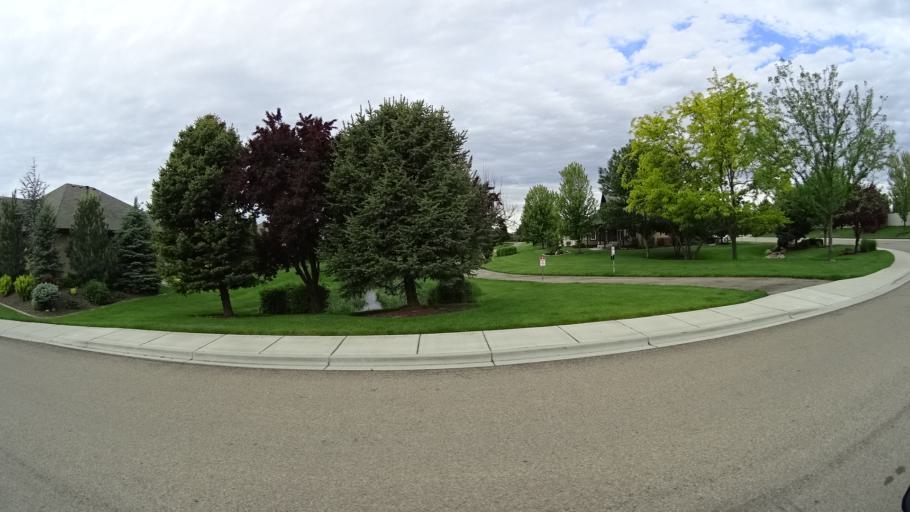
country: US
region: Idaho
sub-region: Ada County
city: Star
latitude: 43.6868
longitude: -116.4986
